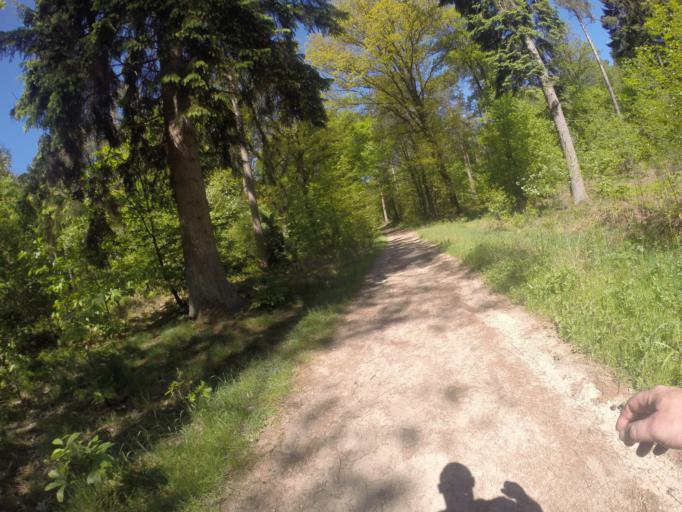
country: NL
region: Gelderland
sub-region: Gemeente Montferland
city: s-Heerenberg
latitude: 51.9104
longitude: 6.2358
